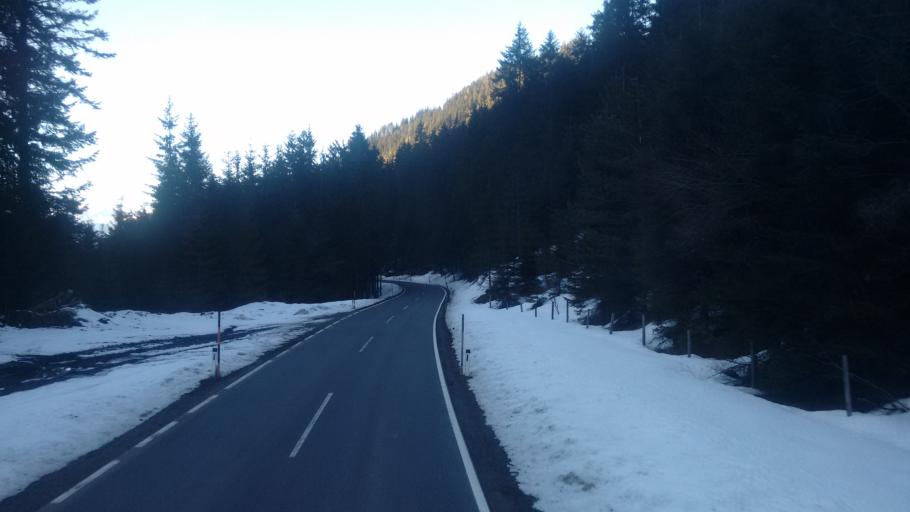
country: AT
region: Salzburg
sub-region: Politischer Bezirk Sankt Johann im Pongau
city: Radstadt
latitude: 47.3296
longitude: 13.4452
